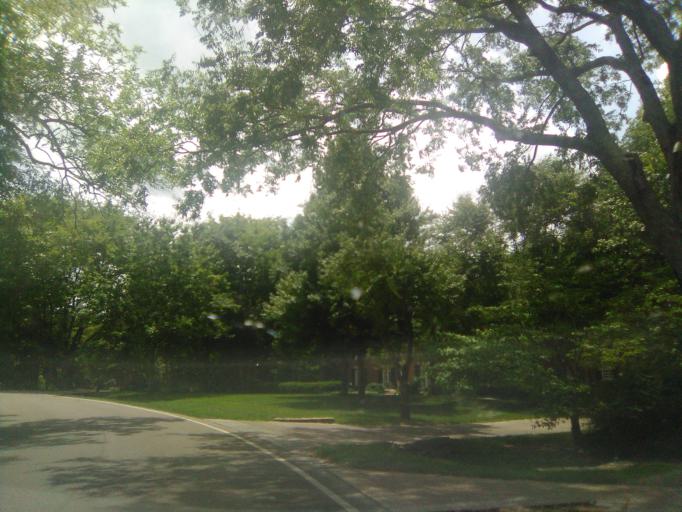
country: US
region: Tennessee
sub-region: Davidson County
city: Belle Meade
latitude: 36.0863
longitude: -86.8594
